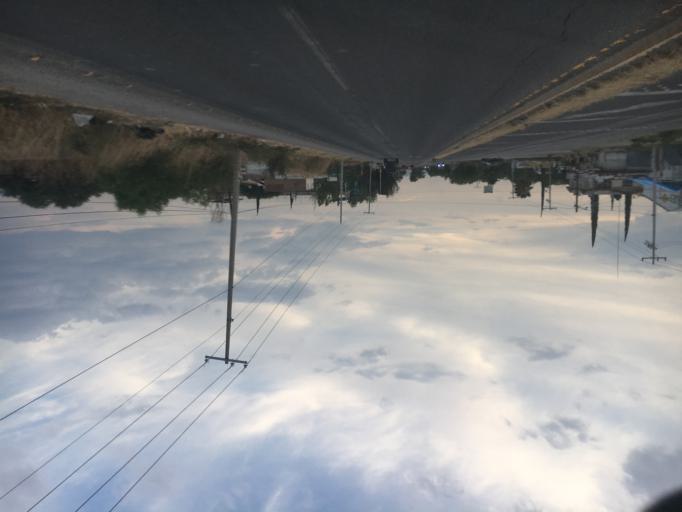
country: MX
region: Guanajuato
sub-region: Leon
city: El CERESO
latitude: 20.9923
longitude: -101.7027
